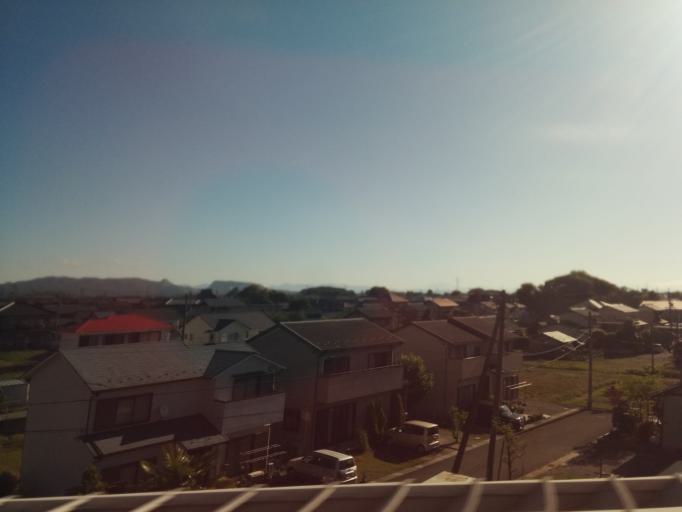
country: JP
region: Gifu
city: Tarui
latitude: 35.3574
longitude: 136.5420
